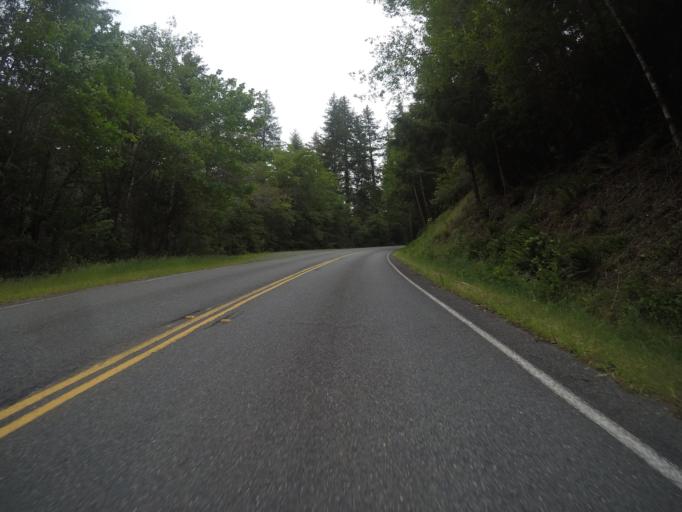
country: US
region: California
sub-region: Del Norte County
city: Bertsch-Oceanview
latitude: 41.7794
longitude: -124.0145
